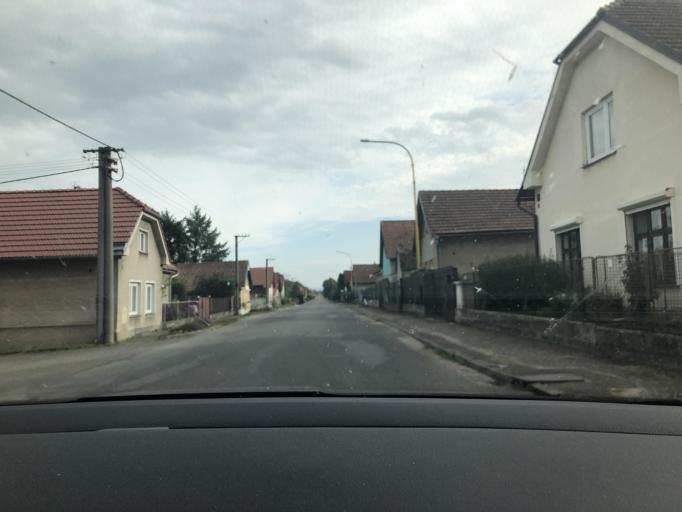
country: CZ
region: Central Bohemia
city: Zizelice
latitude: 50.0981
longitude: 15.4357
